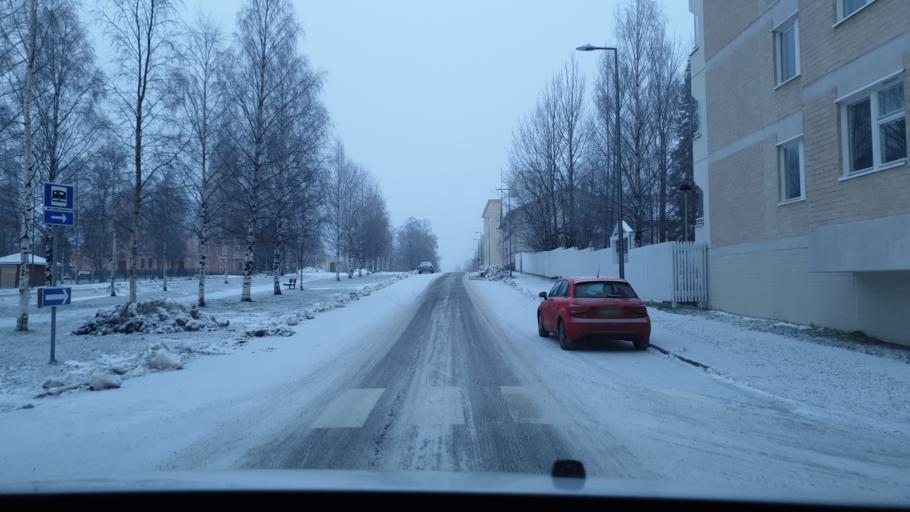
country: FI
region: Lapland
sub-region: Kemi-Tornio
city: Kemi
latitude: 65.7338
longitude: 24.5651
